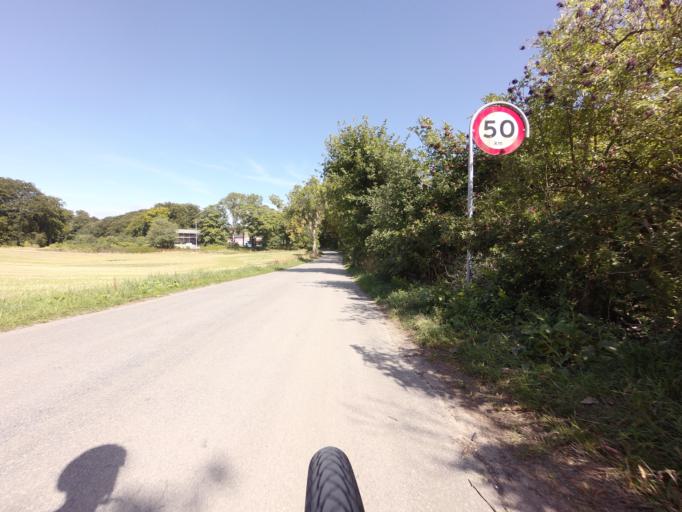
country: DK
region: Zealand
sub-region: Vordingborg Kommune
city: Stege
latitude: 54.9807
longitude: 12.5236
